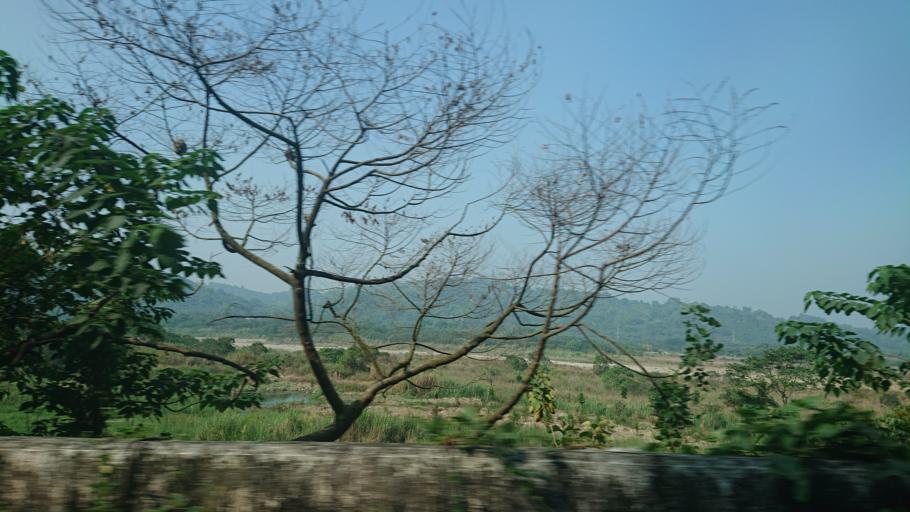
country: TW
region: Taiwan
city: Lugu
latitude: 23.7106
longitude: 120.6658
